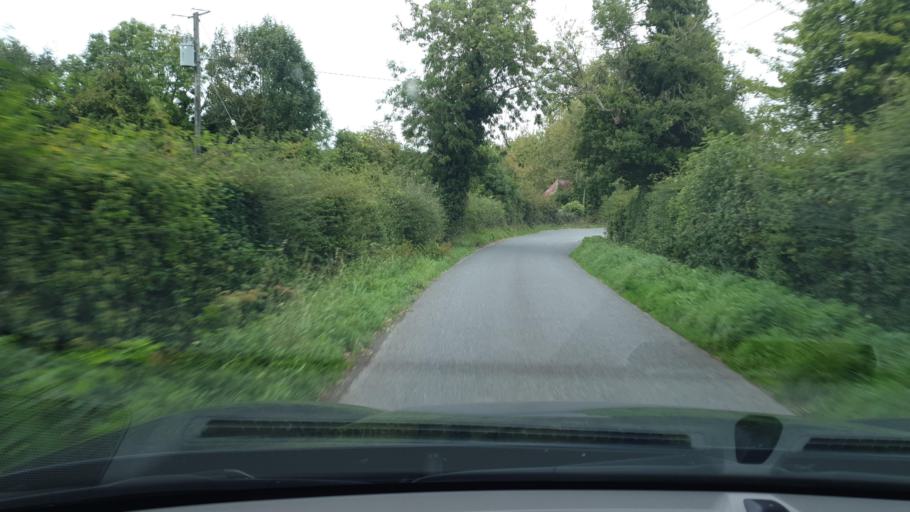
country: IE
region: Leinster
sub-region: An Mhi
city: Ratoath
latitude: 53.4926
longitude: -6.4953
